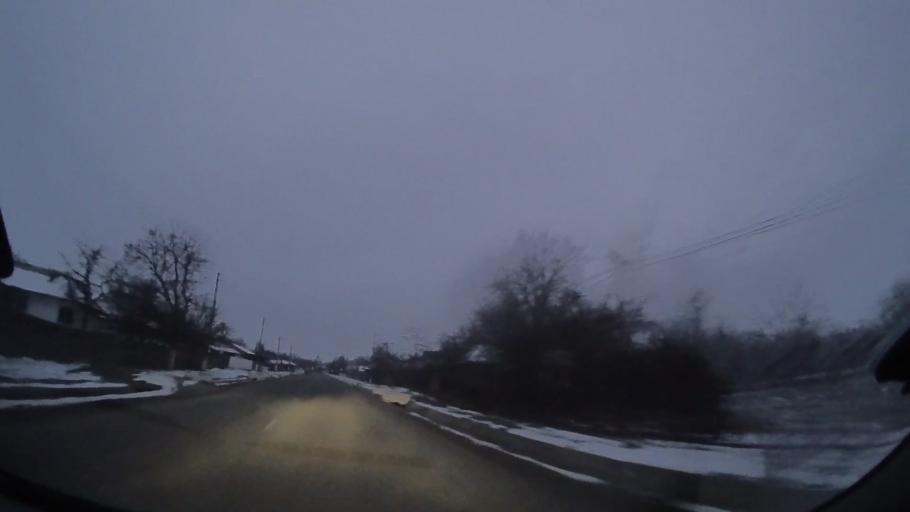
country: RO
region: Vaslui
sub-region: Comuna Dimitrie Cantemir
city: Dimitrie Cantemir
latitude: 46.5043
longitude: 28.0553
